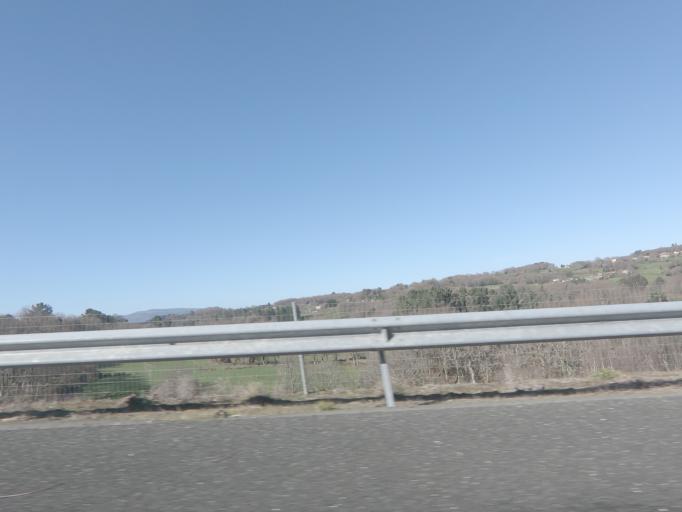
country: ES
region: Galicia
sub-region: Provincia de Pontevedra
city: Lalin
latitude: 42.6115
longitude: -8.1005
